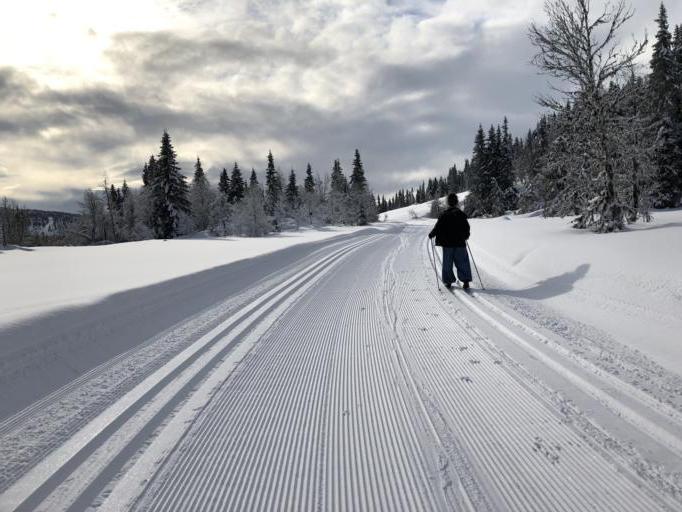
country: NO
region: Oppland
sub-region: Gausdal
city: Segalstad bru
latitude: 61.3201
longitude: 10.0579
